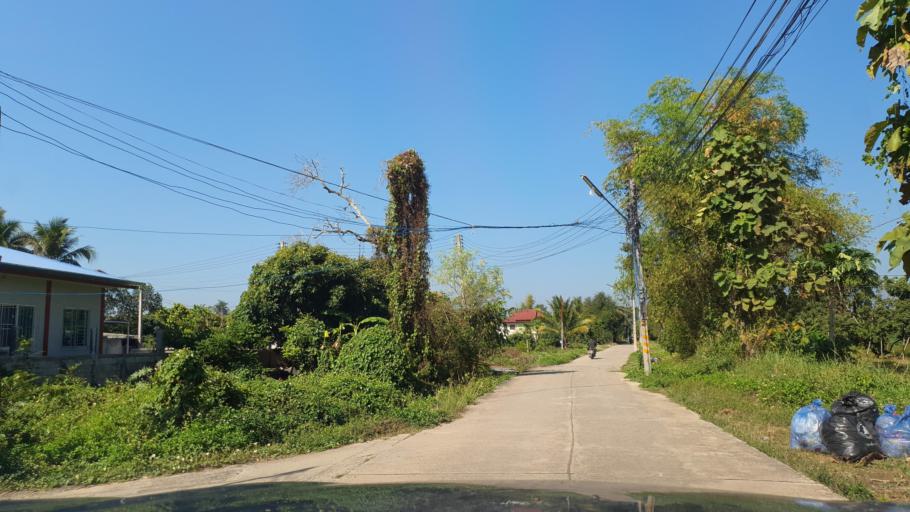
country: TH
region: Chiang Mai
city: Saraphi
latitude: 18.7025
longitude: 99.0732
